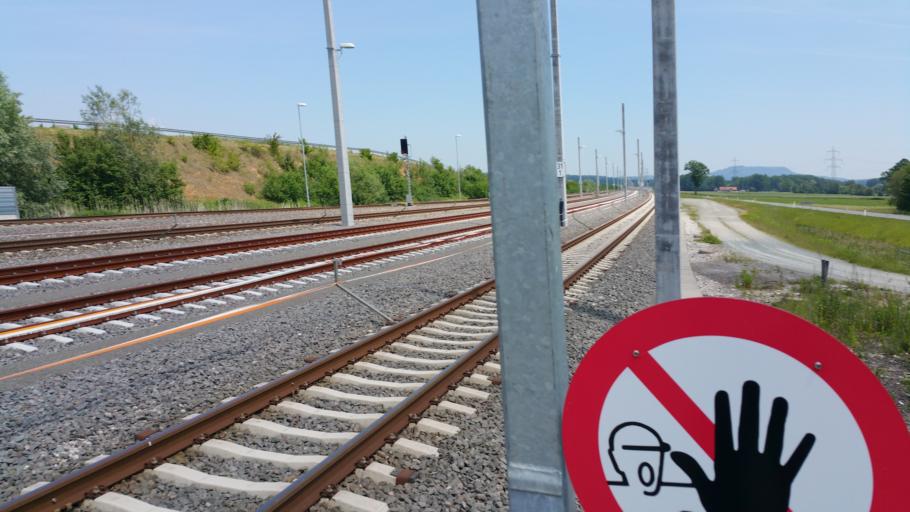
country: AT
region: Styria
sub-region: Politischer Bezirk Deutschlandsberg
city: Wettmannstatten
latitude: 46.8379
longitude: 15.3830
